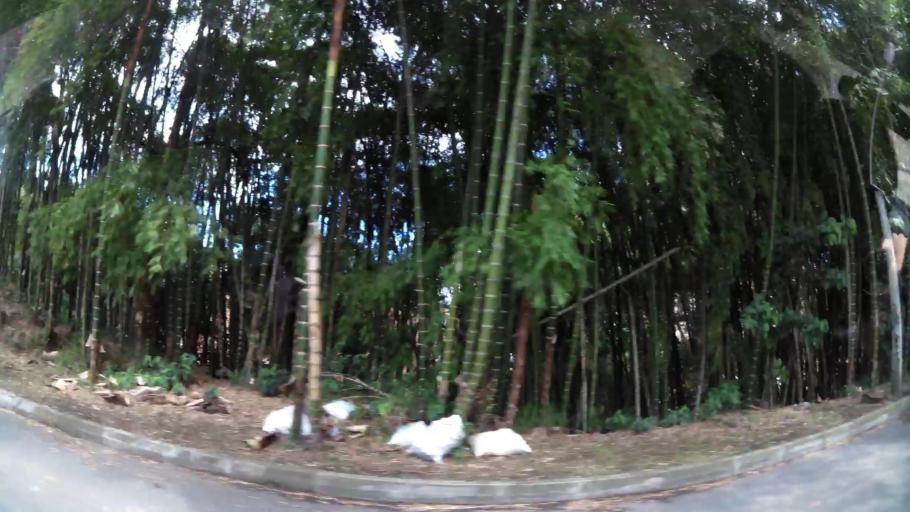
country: CO
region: Antioquia
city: Sabaneta
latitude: 6.1455
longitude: -75.6221
